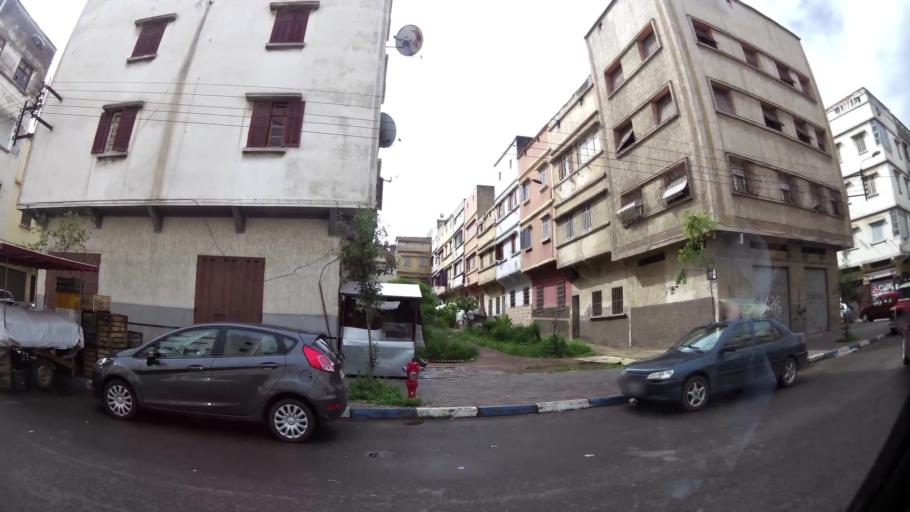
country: MA
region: Grand Casablanca
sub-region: Casablanca
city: Casablanca
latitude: 33.5702
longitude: -7.5895
